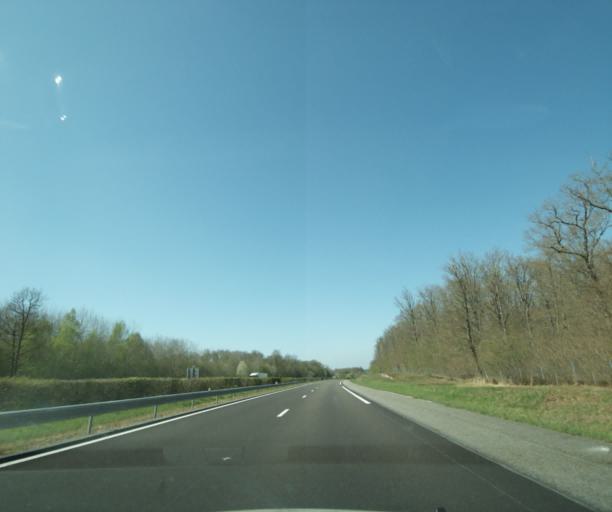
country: FR
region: Bourgogne
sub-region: Departement de la Nievre
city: Neuvy-sur-Loire
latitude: 47.5014
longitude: 2.9252
